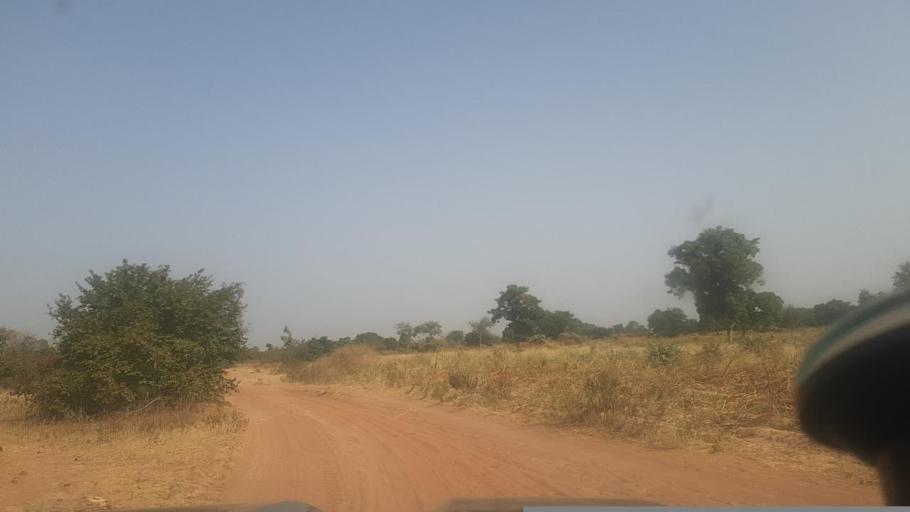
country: ML
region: Segou
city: Bla
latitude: 12.8555
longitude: -5.9756
